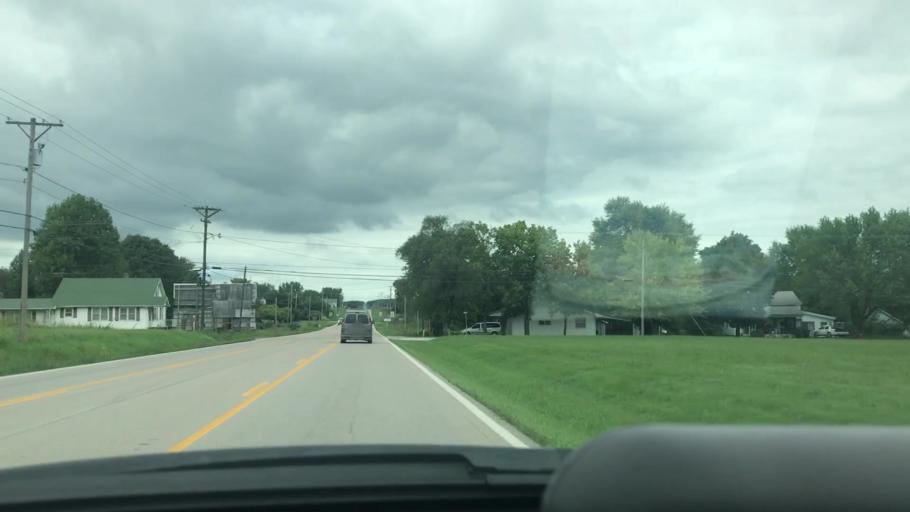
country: US
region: Missouri
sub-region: Dallas County
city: Buffalo
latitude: 37.6470
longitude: -93.1040
